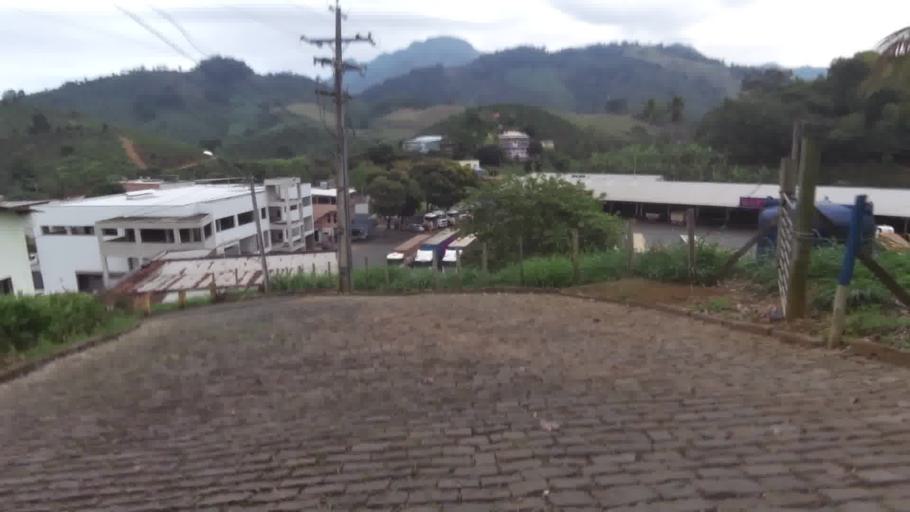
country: BR
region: Espirito Santo
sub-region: Iconha
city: Iconha
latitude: -20.7881
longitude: -40.8192
